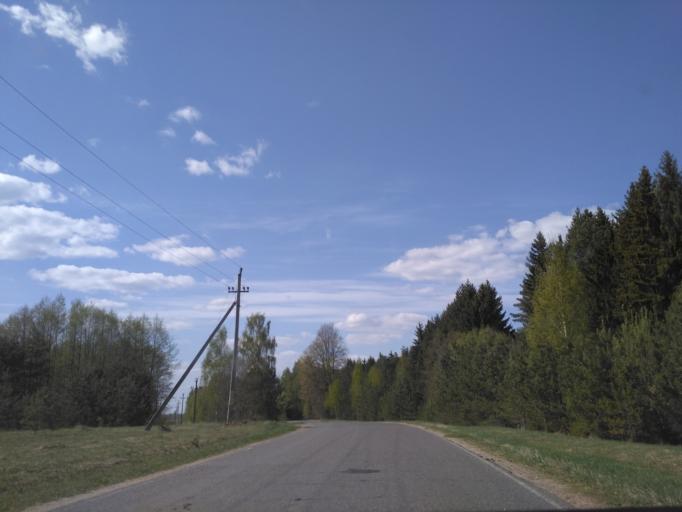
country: BY
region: Minsk
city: Narach
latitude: 54.9615
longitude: 26.6475
